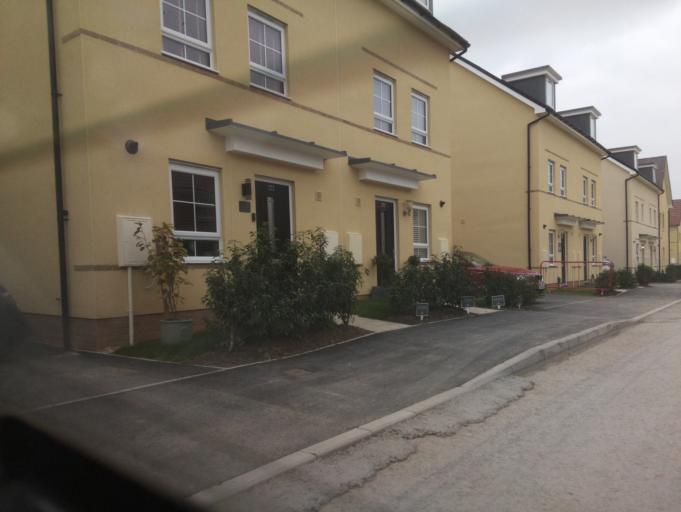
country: GB
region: England
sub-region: South Gloucestershire
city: Thornbury
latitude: 51.6184
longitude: -2.5276
